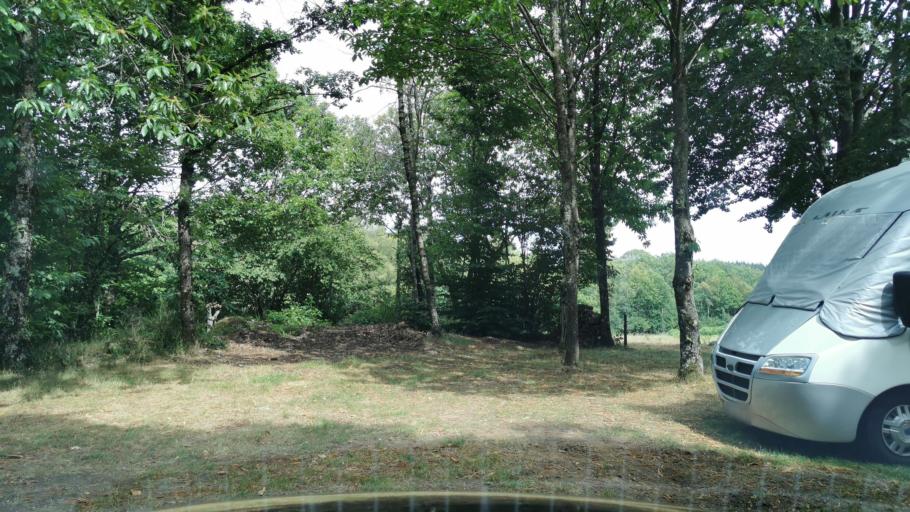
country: FR
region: Bourgogne
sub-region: Departement de Saone-et-Loire
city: Etang-sur-Arroux
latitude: 46.8066
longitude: 4.2610
